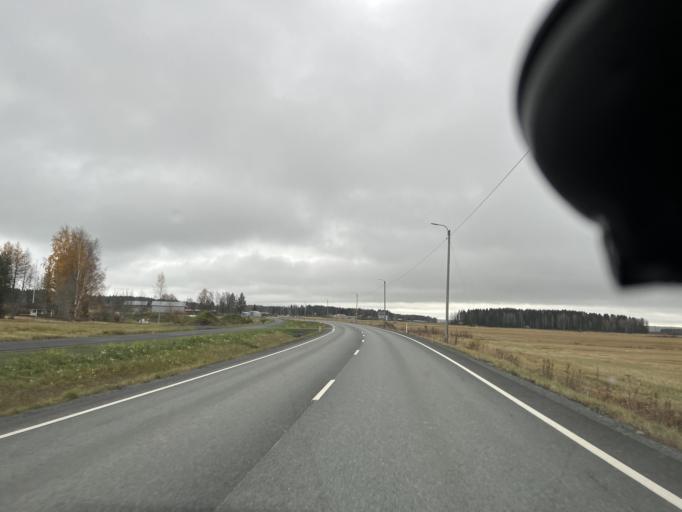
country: FI
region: Northern Ostrobothnia
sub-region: Ylivieska
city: Sievi
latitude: 63.9549
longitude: 24.5085
